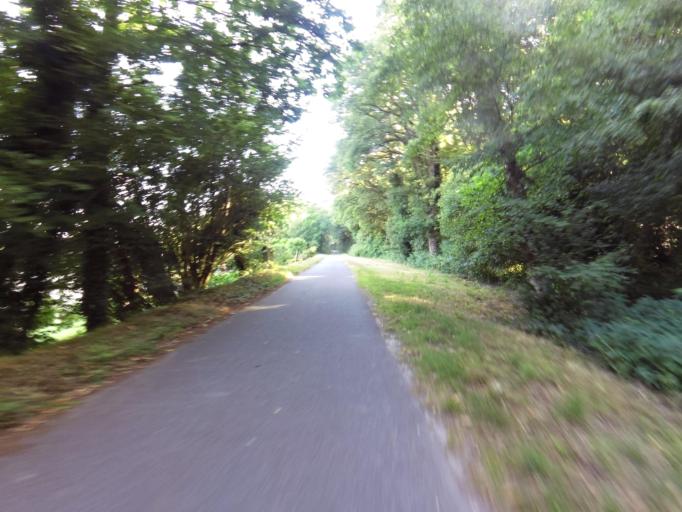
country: FR
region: Brittany
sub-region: Departement du Morbihan
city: Guillac
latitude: 47.9053
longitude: -2.4323
